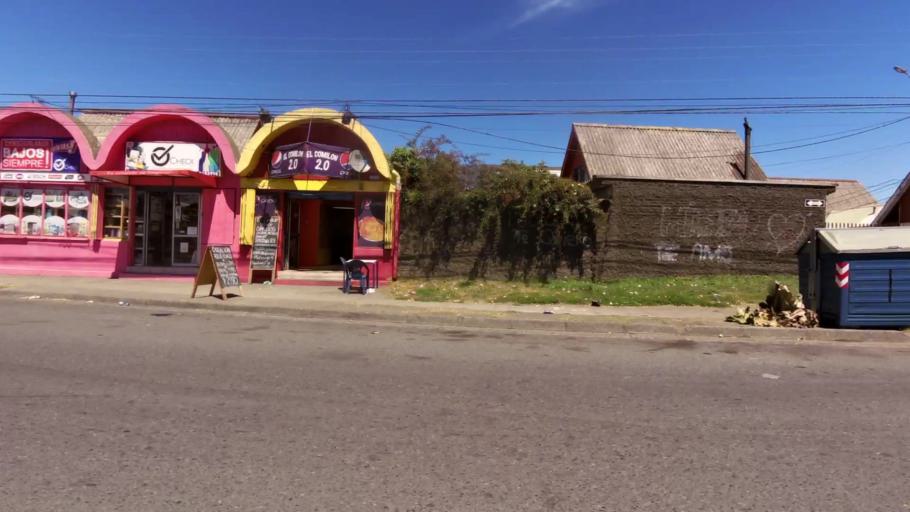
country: CL
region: Biobio
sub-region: Provincia de Concepcion
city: Talcahuano
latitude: -36.7596
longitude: -73.0855
